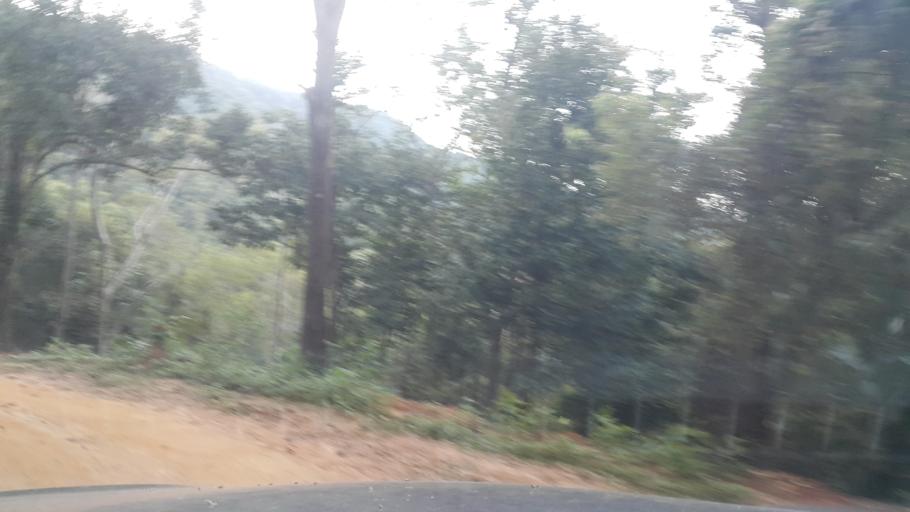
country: TH
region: Chiang Mai
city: Samoeng
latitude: 19.0085
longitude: 98.6675
